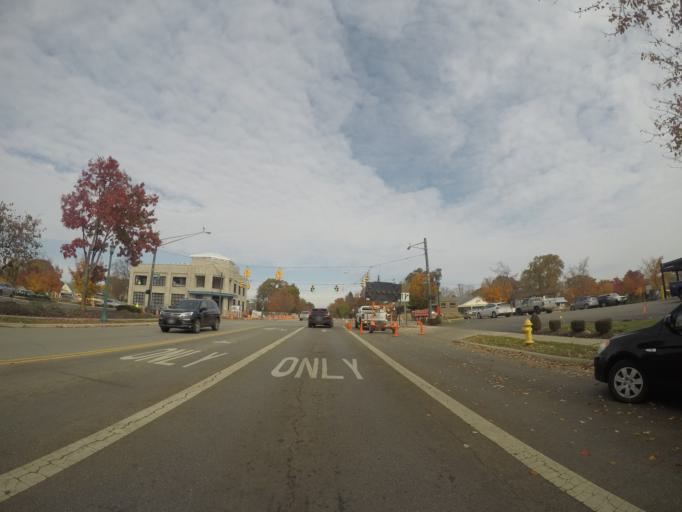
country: US
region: Ohio
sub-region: Franklin County
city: Upper Arlington
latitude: 40.0072
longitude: -83.0584
